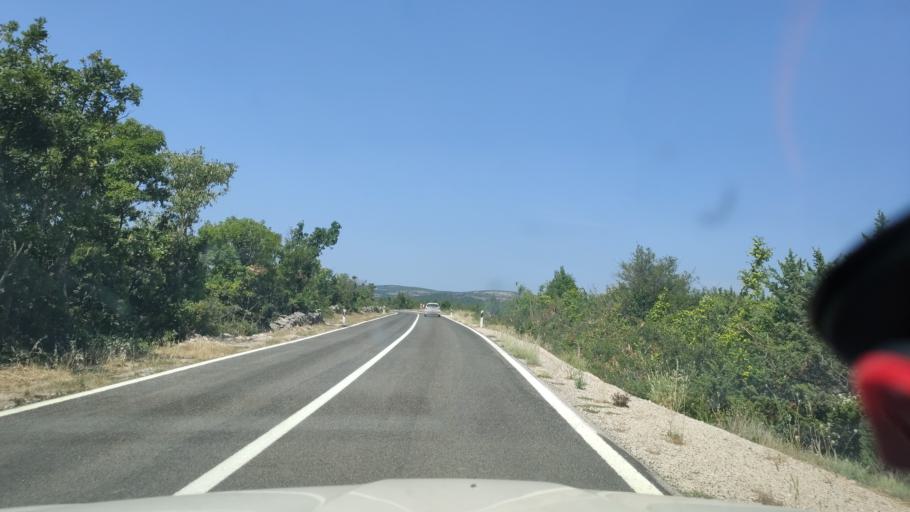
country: HR
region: Sibensko-Kniniska
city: Kistanje
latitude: 43.9719
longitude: 15.9000
